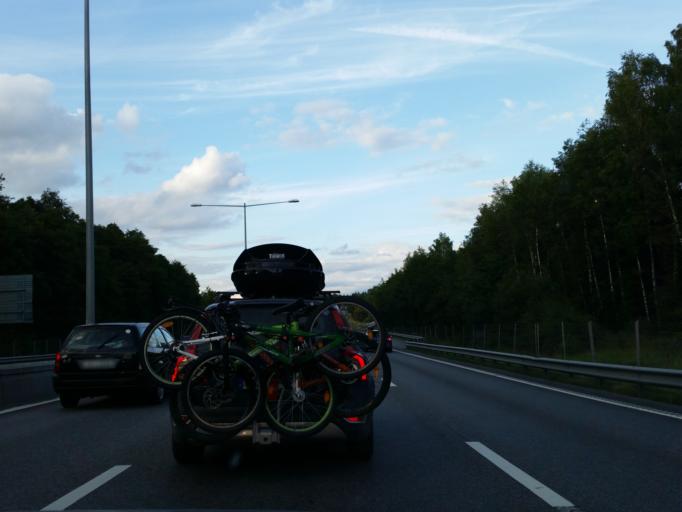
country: SE
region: Stockholm
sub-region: Botkyrka Kommun
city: Eriksberg
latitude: 59.2330
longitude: 17.8069
